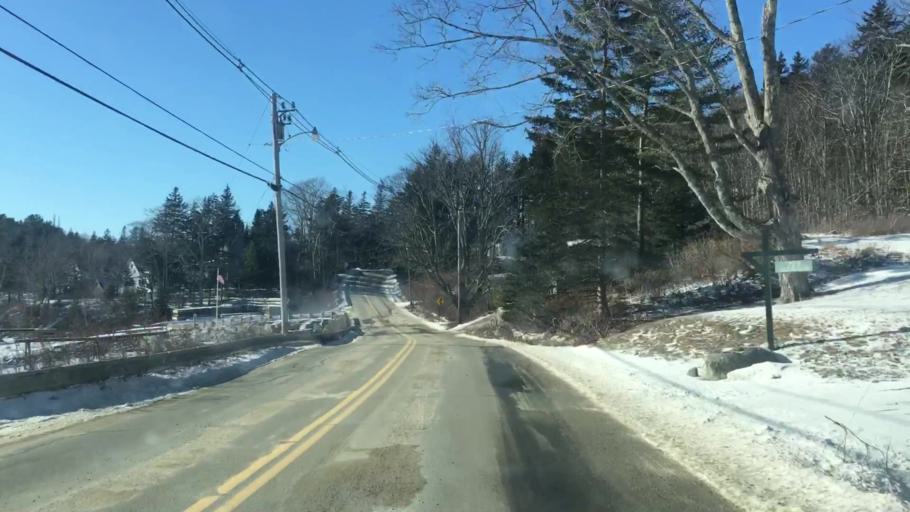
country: US
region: Maine
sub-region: Hancock County
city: Castine
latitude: 44.3421
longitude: -68.7401
